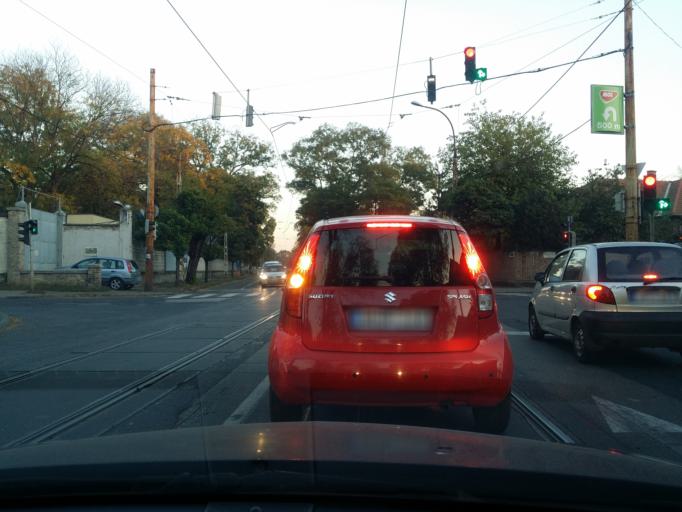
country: HU
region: Budapest
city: Budapest XV. keruelet
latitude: 47.5689
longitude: 19.1171
